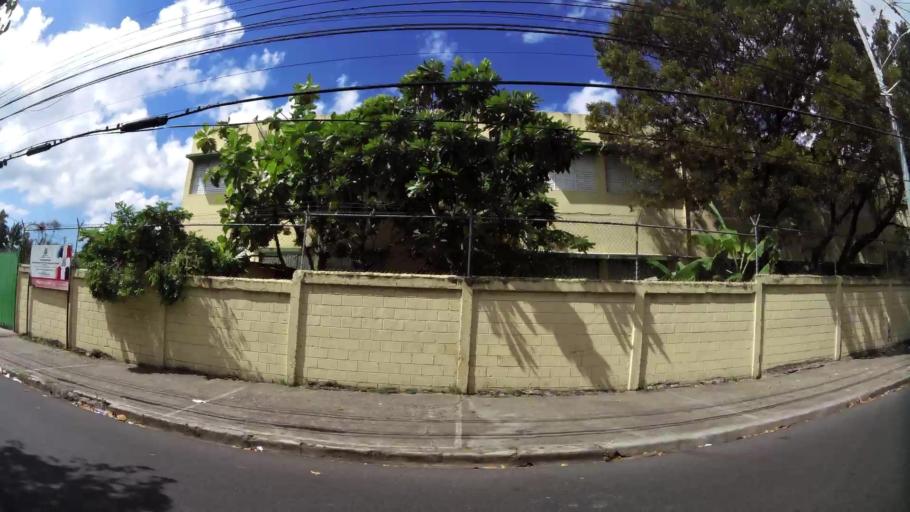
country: DO
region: Nacional
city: Ensanche Luperon
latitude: 18.4923
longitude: -69.8874
